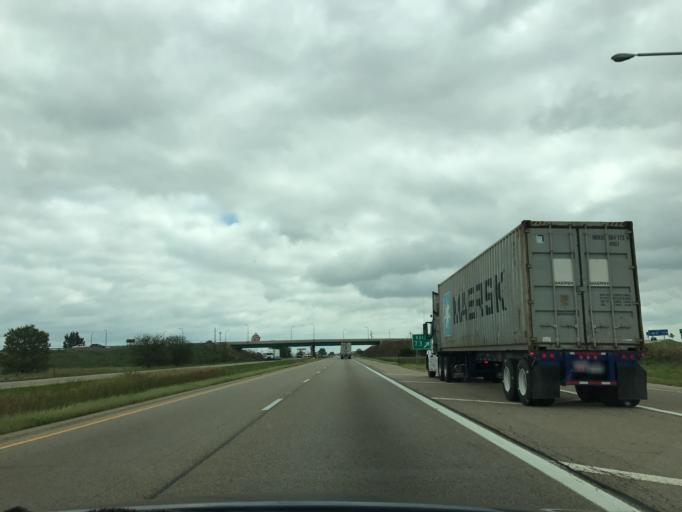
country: US
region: Illinois
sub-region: LaSalle County
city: Peru
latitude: 41.3647
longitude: -89.1556
